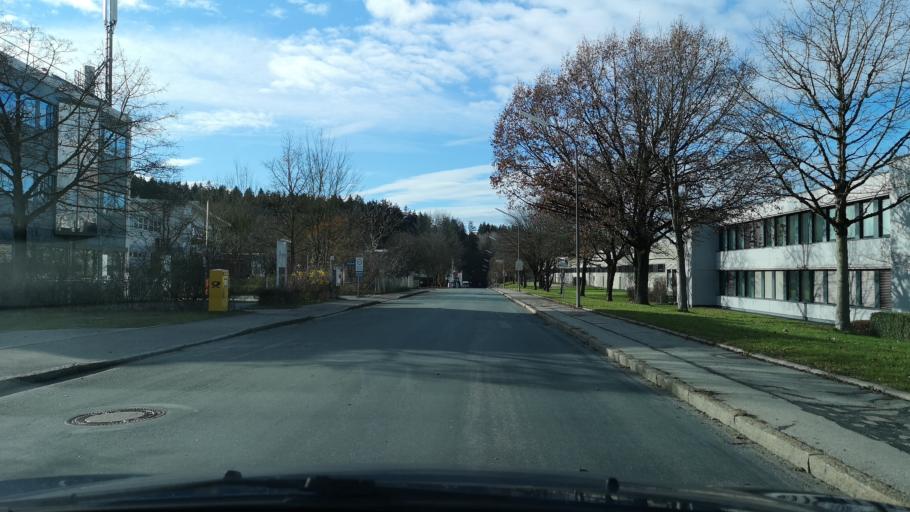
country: DE
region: Bavaria
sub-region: Upper Bavaria
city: Ebersberg
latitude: 48.0966
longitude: 11.9610
